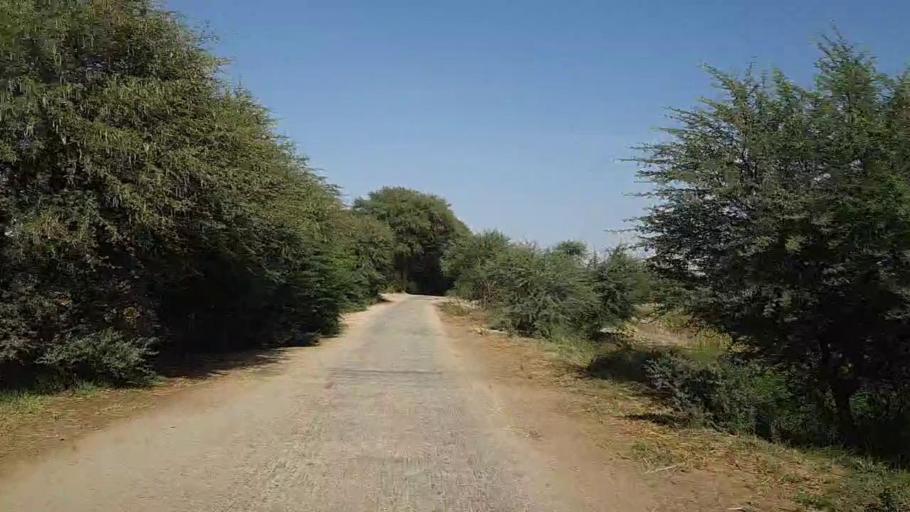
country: PK
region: Sindh
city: Kotri
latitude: 25.1719
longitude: 68.2999
